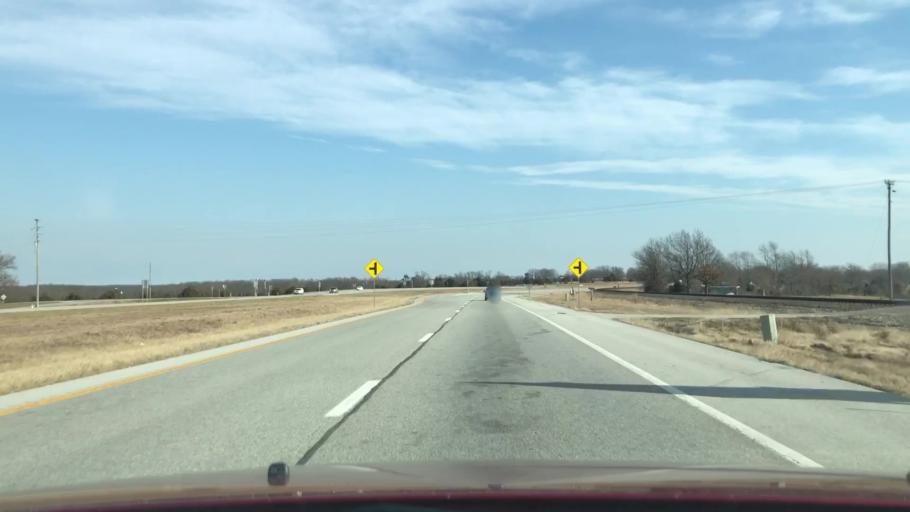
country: US
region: Missouri
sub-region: Webster County
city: Seymour
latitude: 37.1709
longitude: -92.8652
